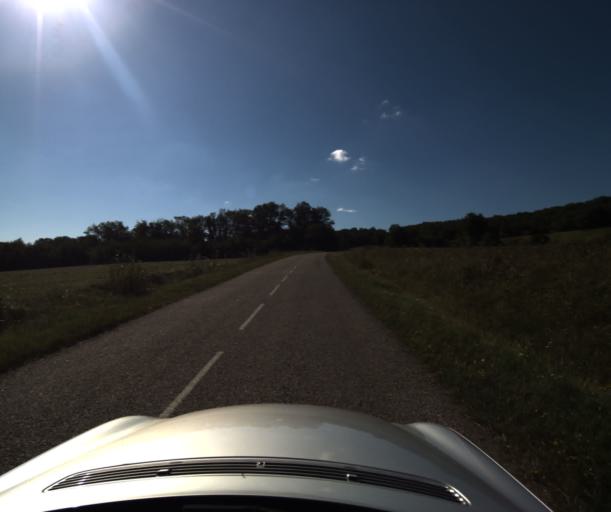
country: FR
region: Midi-Pyrenees
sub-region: Departement de l'Ariege
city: Belesta
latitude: 42.9786
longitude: 1.9185
